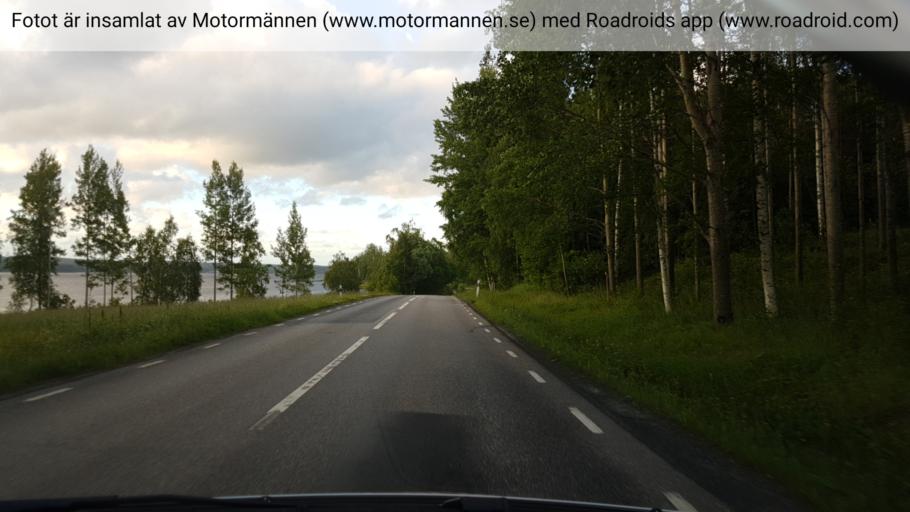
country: SE
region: OErebro
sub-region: Nora Kommun
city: As
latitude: 59.4785
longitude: 14.9186
